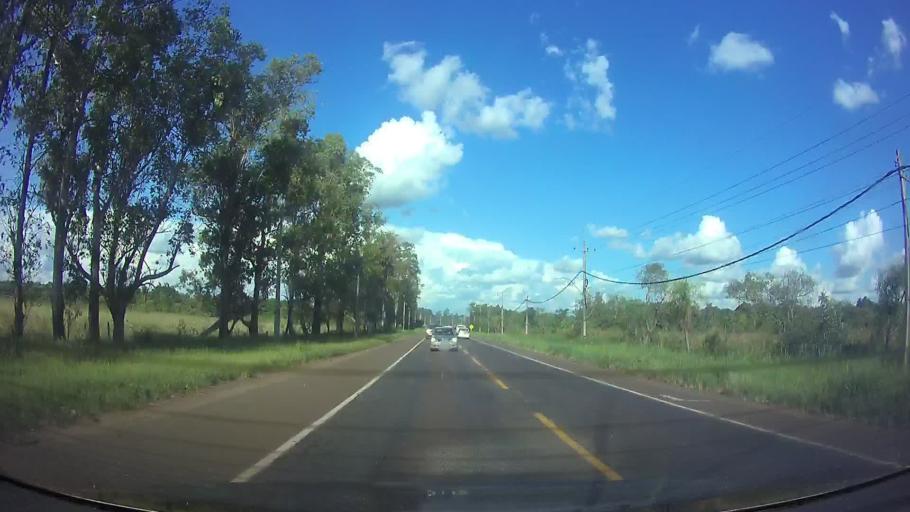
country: PY
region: Cordillera
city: Eusebio Ayala
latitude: -25.3807
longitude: -56.9920
